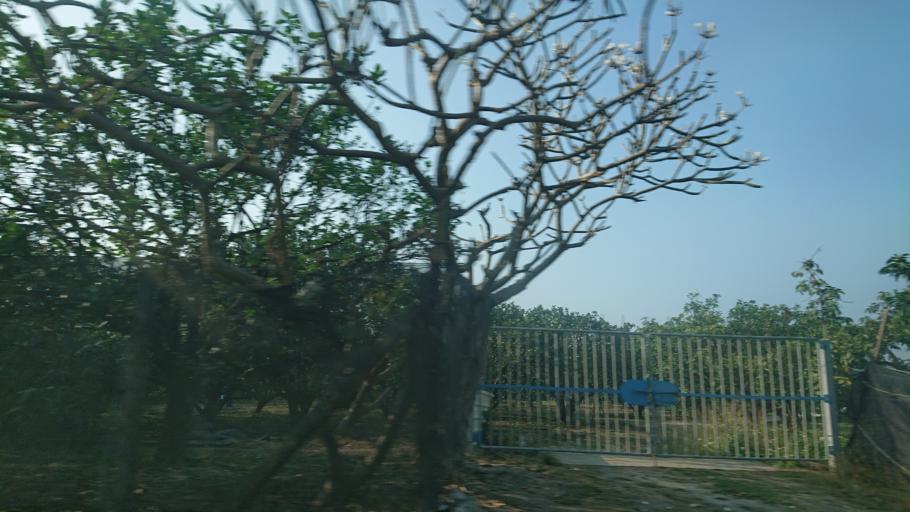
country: TW
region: Taiwan
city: Xinying
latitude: 23.1805
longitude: 120.2647
